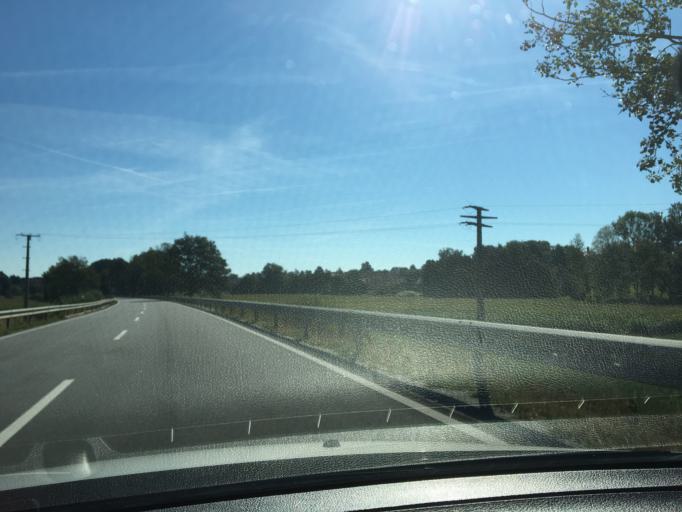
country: DE
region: Bavaria
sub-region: Lower Bavaria
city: Velden
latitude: 48.3704
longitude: 12.2521
